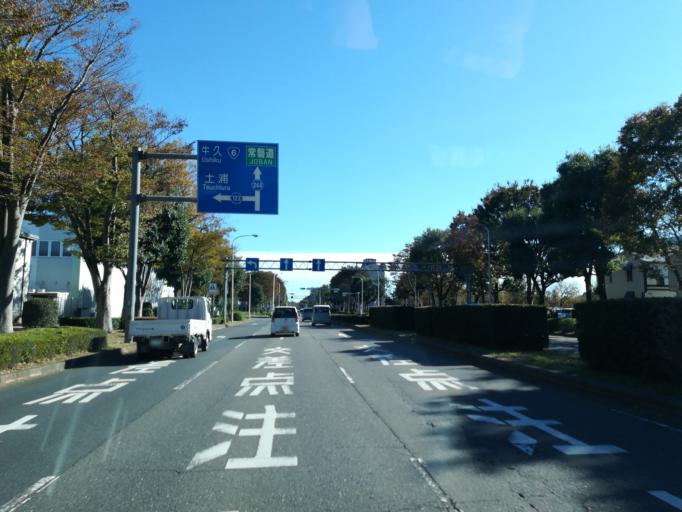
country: JP
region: Ibaraki
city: Naka
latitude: 36.0730
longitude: 140.1131
